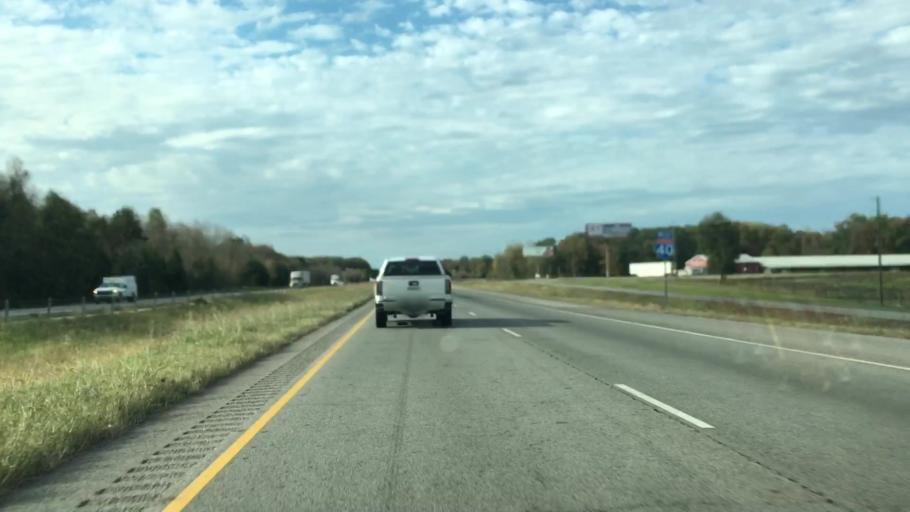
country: US
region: Arkansas
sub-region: Pope County
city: Atkins
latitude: 35.2236
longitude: -92.8355
